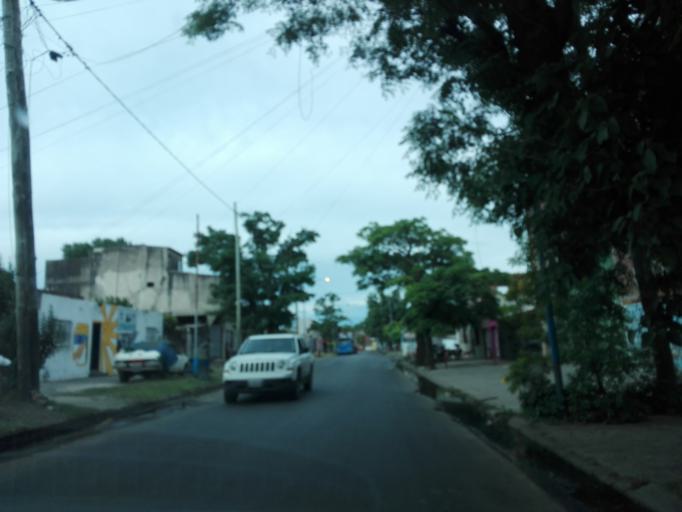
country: AR
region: Buenos Aires
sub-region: Partido de Lanus
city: Lanus
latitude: -34.7058
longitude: -58.3698
